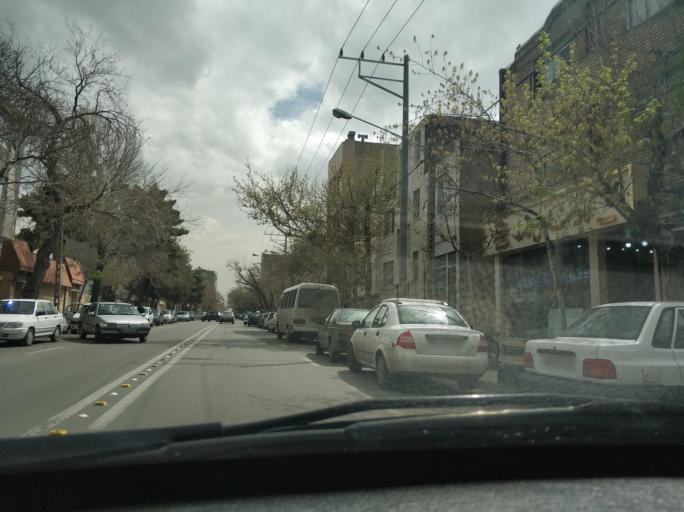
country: IR
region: Razavi Khorasan
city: Mashhad
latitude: 36.2822
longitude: 59.5726
